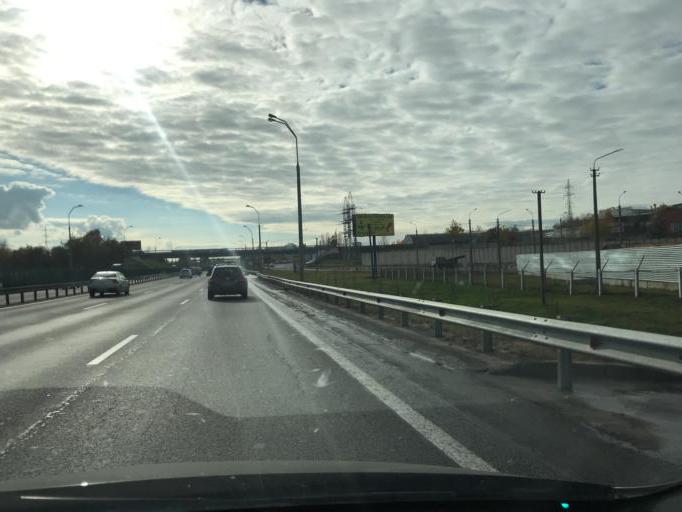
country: BY
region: Minsk
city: Vyaliki Trastsyanets
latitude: 53.8524
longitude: 27.6743
